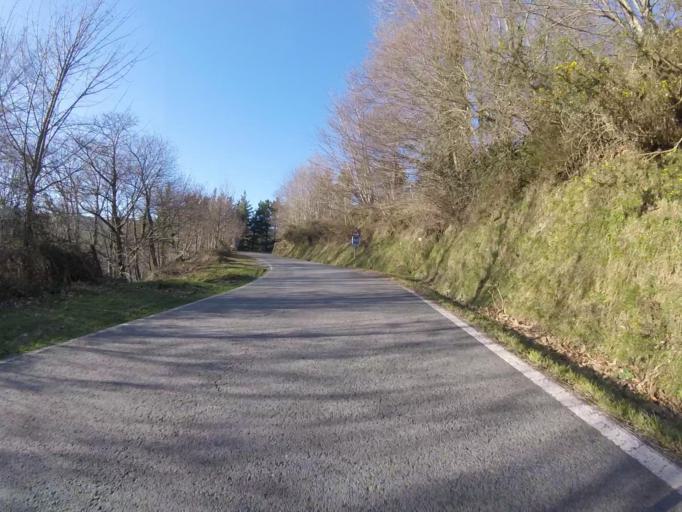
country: ES
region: Navarre
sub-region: Provincia de Navarra
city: Lesaka
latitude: 43.2650
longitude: -1.7404
